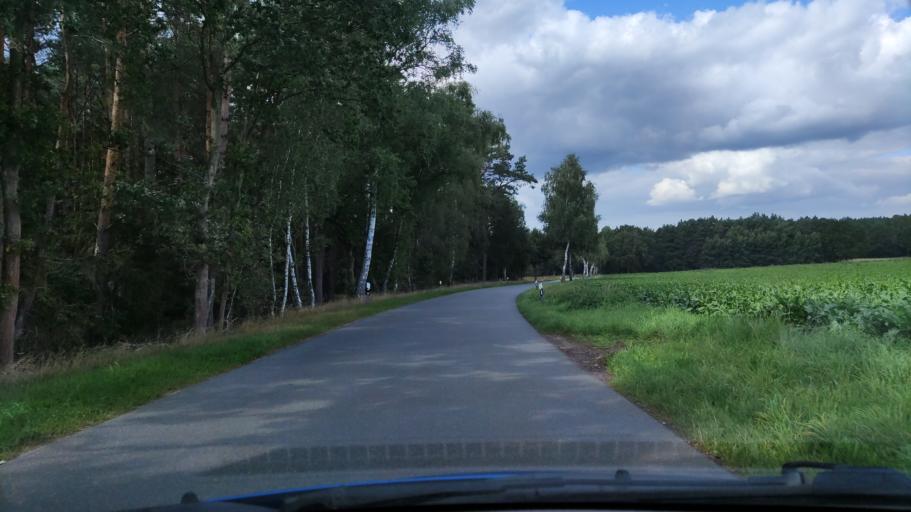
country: DE
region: Lower Saxony
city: Weste
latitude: 53.0353
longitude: 10.7217
